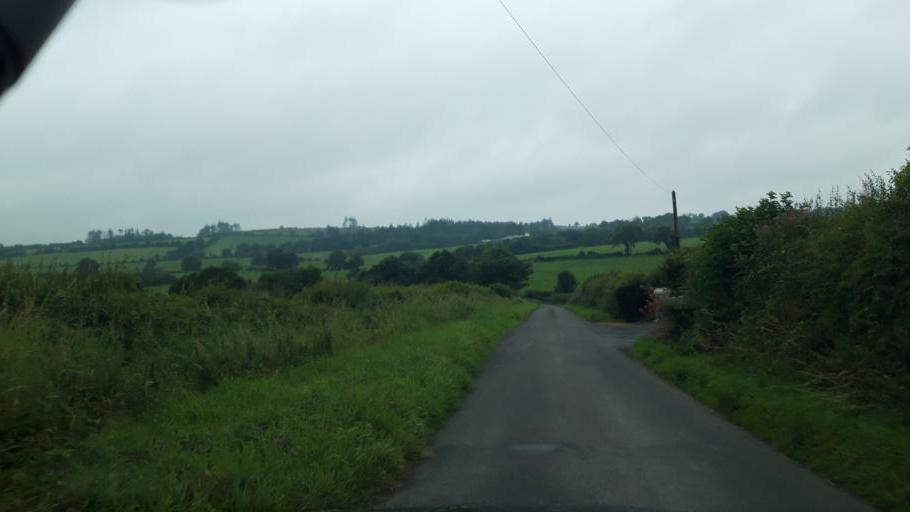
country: IE
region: Leinster
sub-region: Kilkenny
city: Callan
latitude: 52.6410
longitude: -7.5046
